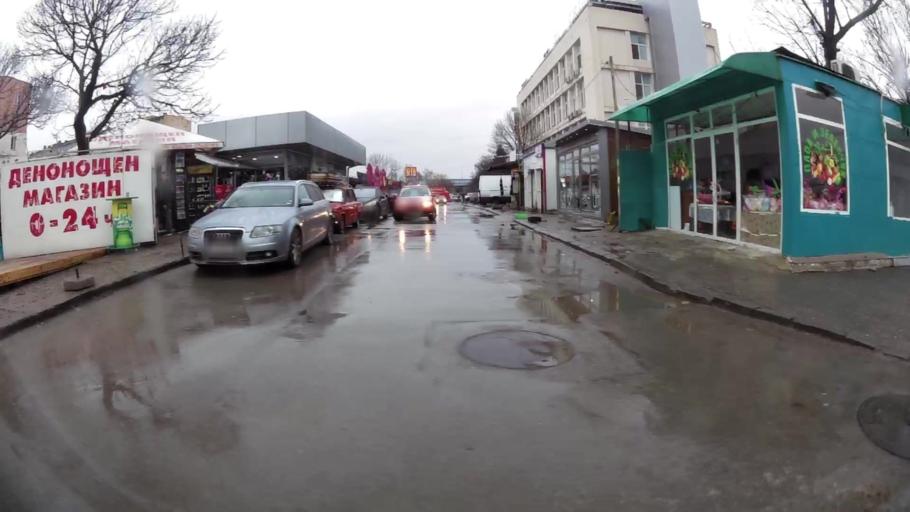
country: BG
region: Sofia-Capital
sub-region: Stolichna Obshtina
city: Sofia
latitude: 42.6681
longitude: 23.3957
